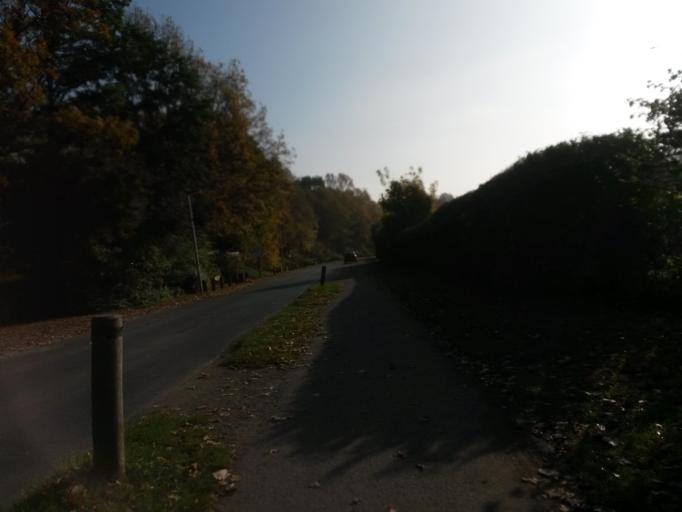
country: DE
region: Bremen
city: Bremen
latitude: 53.0653
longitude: 8.8182
